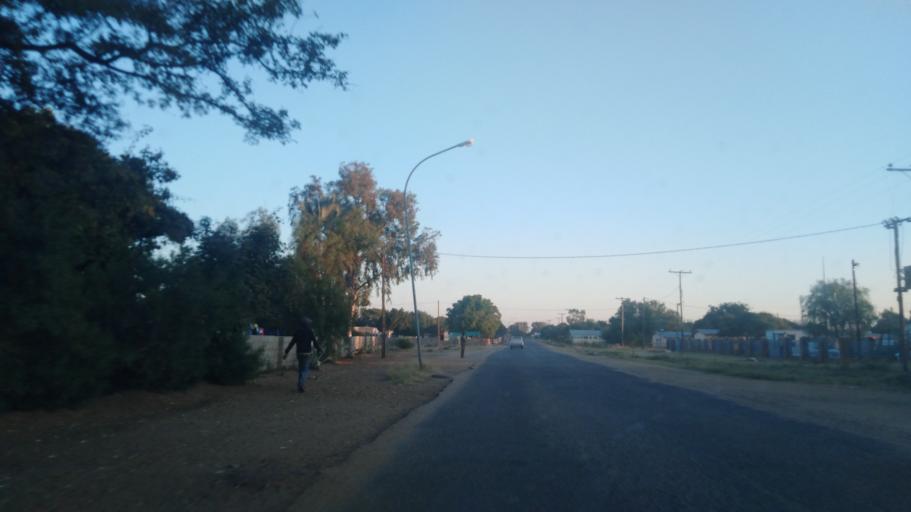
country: BW
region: Central
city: Mahalapye
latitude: -23.1153
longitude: 26.8293
